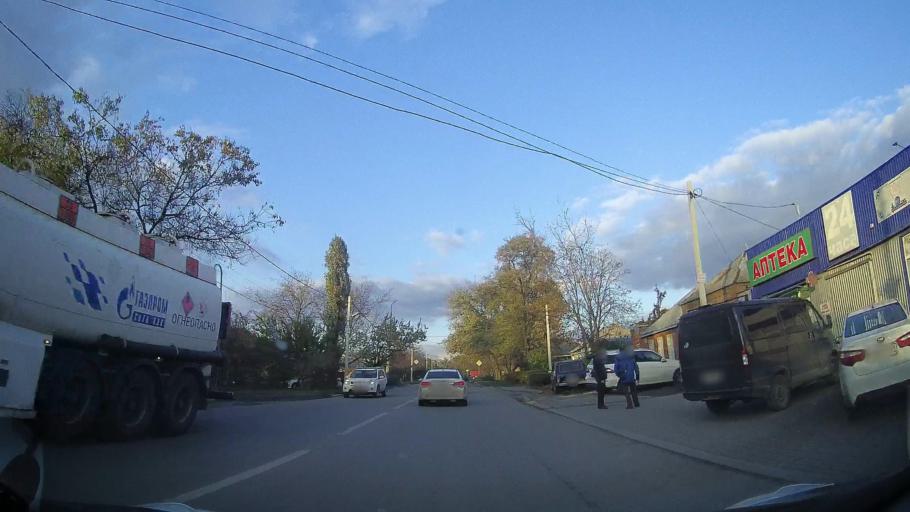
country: RU
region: Rostov
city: Imeni Chkalova
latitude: 47.2643
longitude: 39.7768
